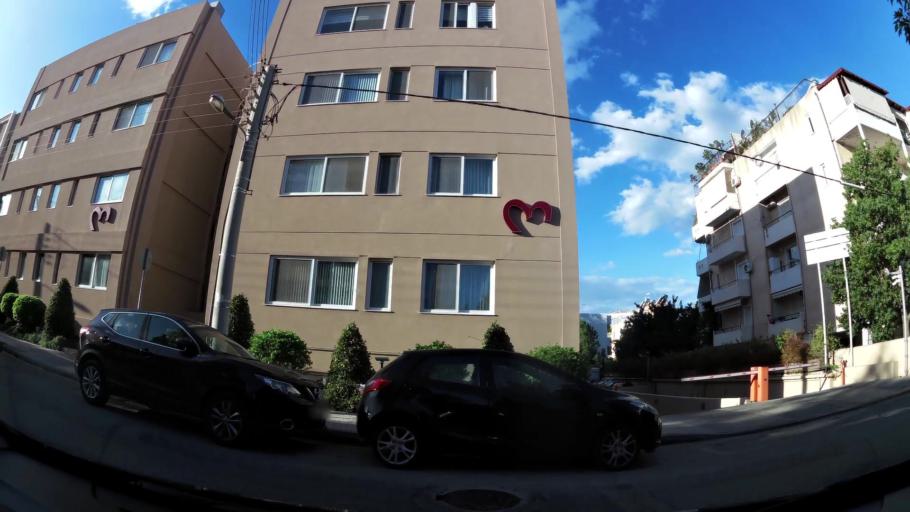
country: GR
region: Attica
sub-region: Nomarchia Athinas
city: Elliniko
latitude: 37.8860
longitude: 23.7470
